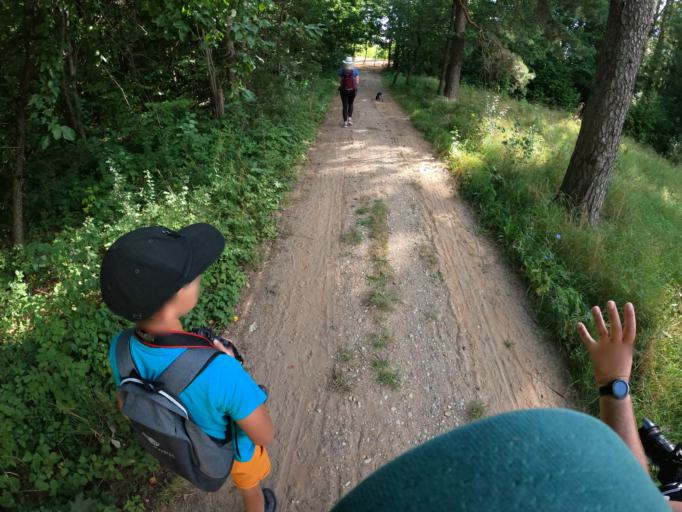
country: LV
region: Priekule
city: Priekule
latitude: 56.3675
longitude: 21.6102
